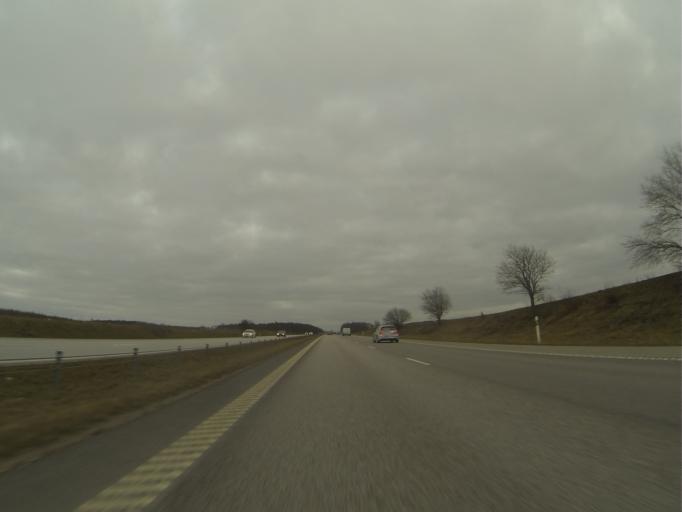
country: SE
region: Skane
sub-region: Malmo
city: Oxie
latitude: 55.5489
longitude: 13.1317
